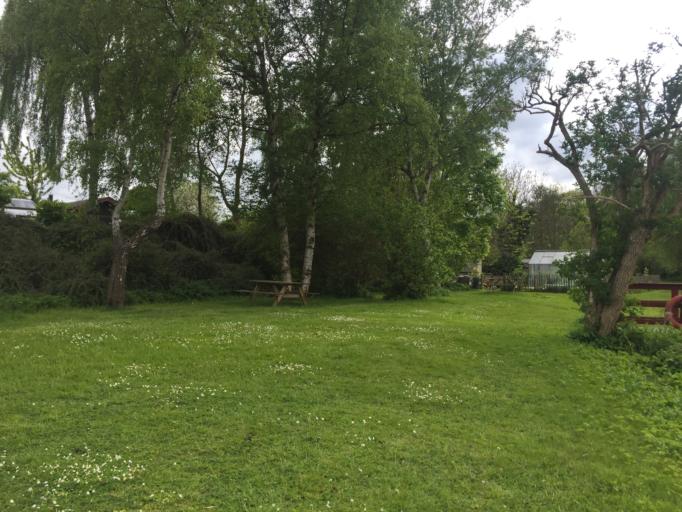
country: DK
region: Capital Region
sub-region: Kobenhavn
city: Christianshavn
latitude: 55.6795
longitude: 12.6143
